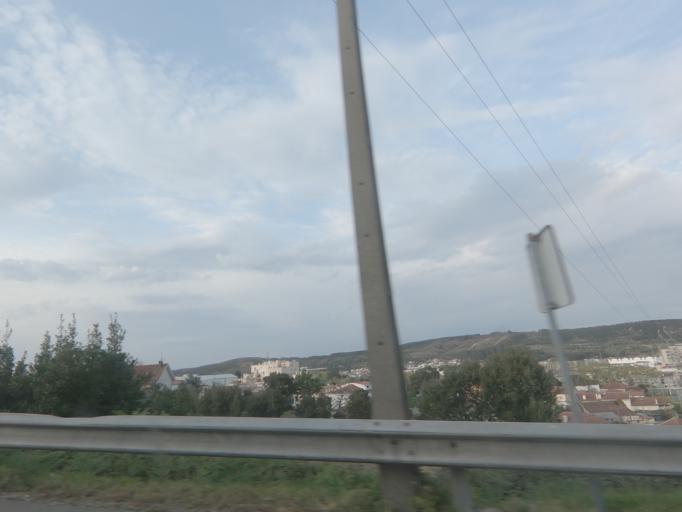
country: PT
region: Porto
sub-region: Valongo
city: Valongo
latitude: 41.1914
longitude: -8.5073
